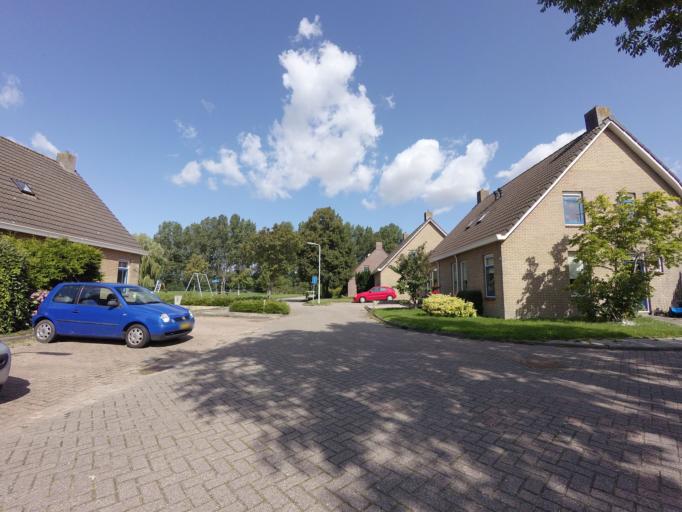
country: NL
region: Friesland
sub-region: Gemeente Het Bildt
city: Sint Annaparochie
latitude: 53.2810
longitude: 5.7017
